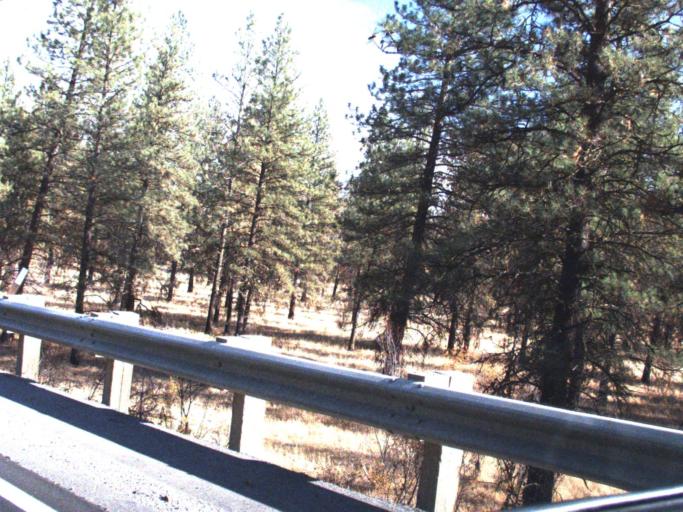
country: US
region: Washington
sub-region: Stevens County
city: Kettle Falls
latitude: 48.5883
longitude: -118.1485
